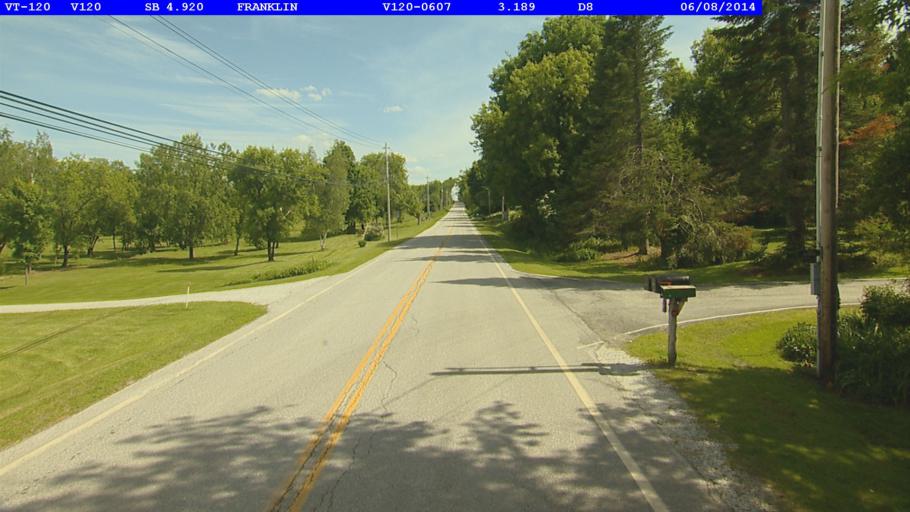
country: US
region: Vermont
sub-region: Franklin County
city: Enosburg Falls
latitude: 44.9781
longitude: -72.9138
